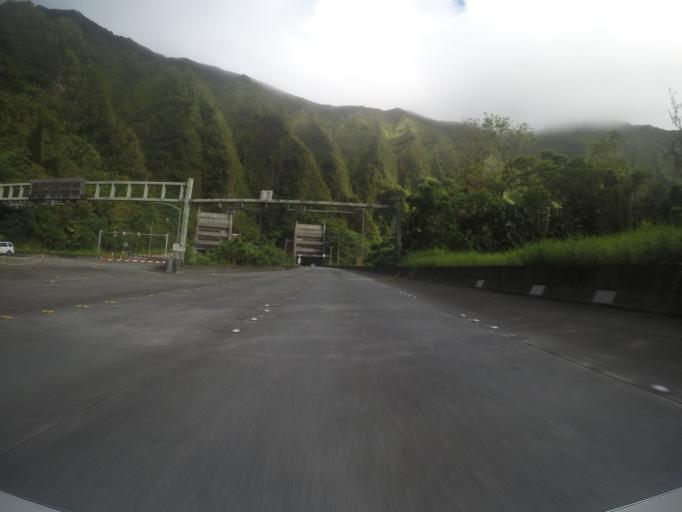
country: US
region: Hawaii
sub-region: Honolulu County
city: Kane'ohe
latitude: 21.4035
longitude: -157.8331
